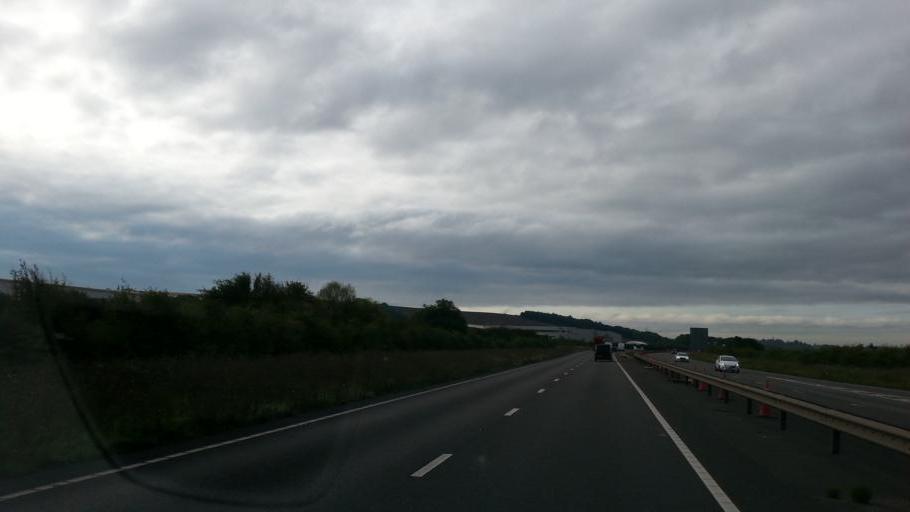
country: GB
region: England
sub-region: Lincolnshire
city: Great Gonerby
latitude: 52.9480
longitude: -0.6826
